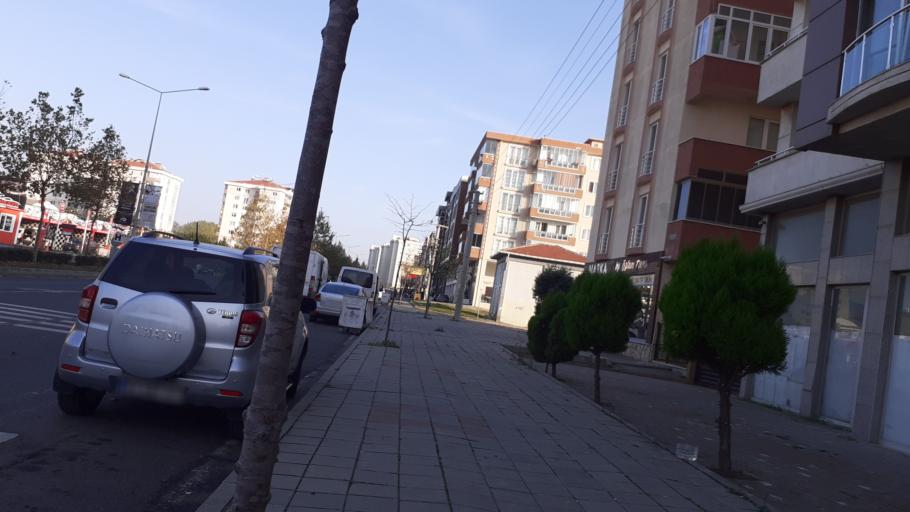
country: TR
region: Tekirdag
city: Corlu
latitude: 41.1490
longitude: 27.8294
